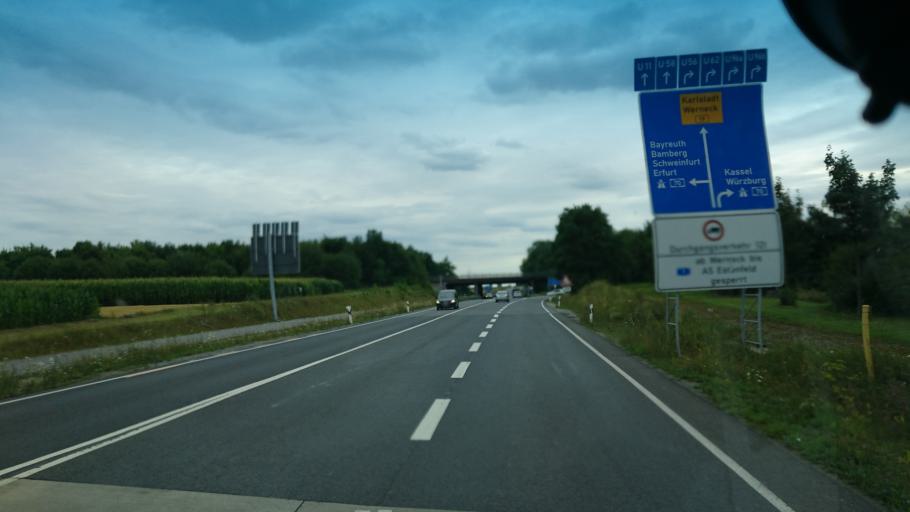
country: DE
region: Bavaria
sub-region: Regierungsbezirk Unterfranken
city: Werneck
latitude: 50.0038
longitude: 10.1202
